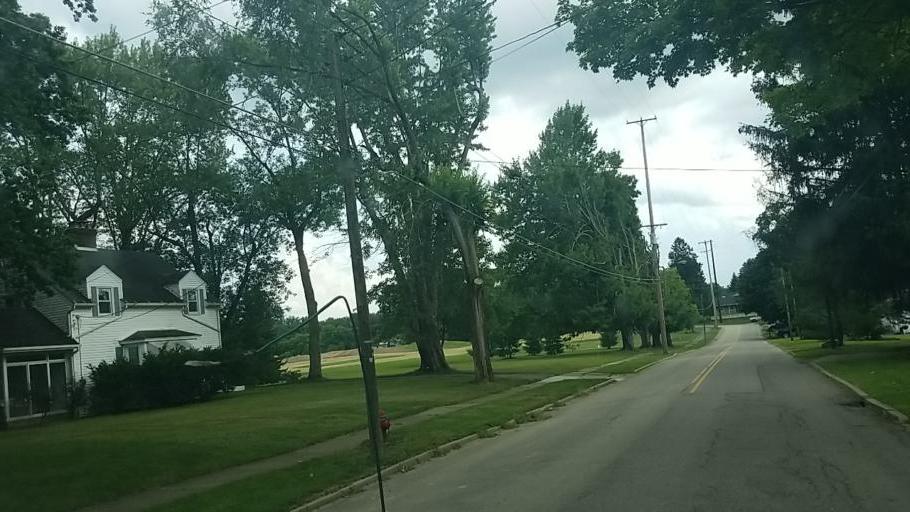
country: US
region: Ohio
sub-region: Medina County
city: Westfield Center
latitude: 41.0224
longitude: -81.9336
